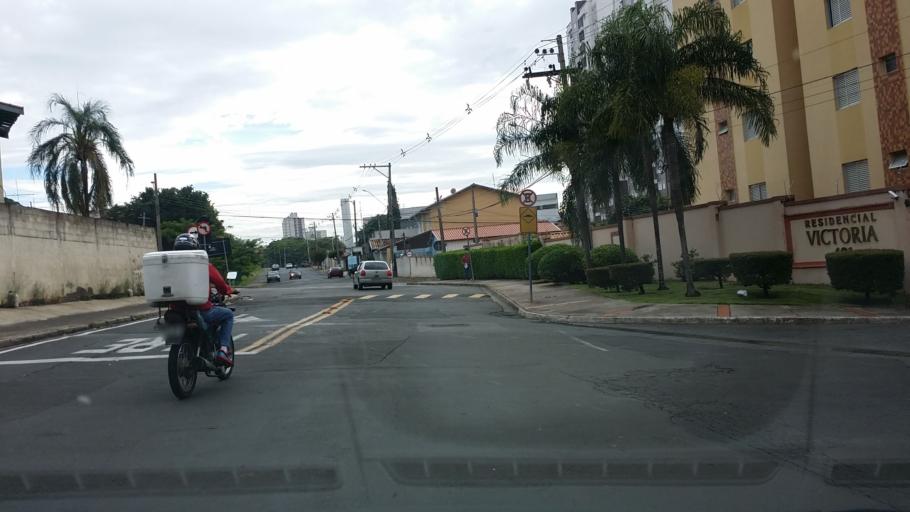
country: BR
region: Sao Paulo
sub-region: Indaiatuba
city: Indaiatuba
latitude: -23.0949
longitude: -47.2205
